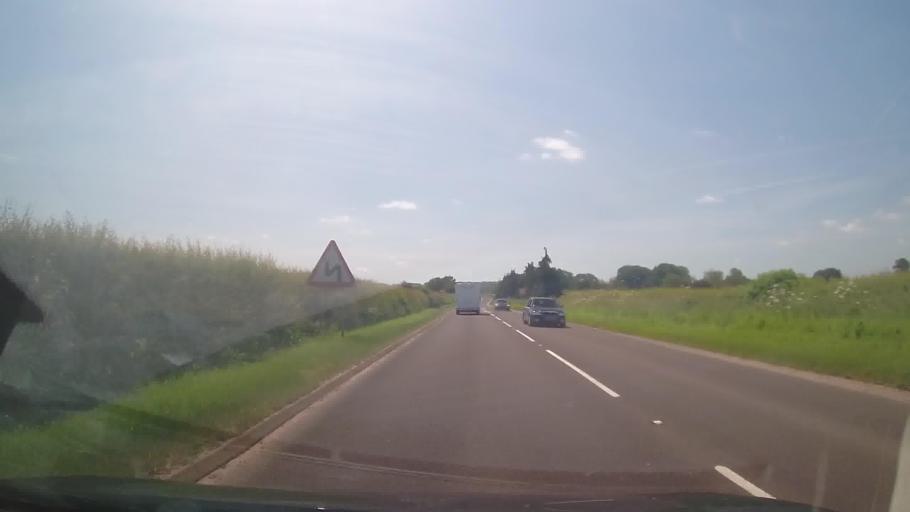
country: GB
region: England
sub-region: Herefordshire
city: Orleton
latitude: 52.3202
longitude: -2.7097
